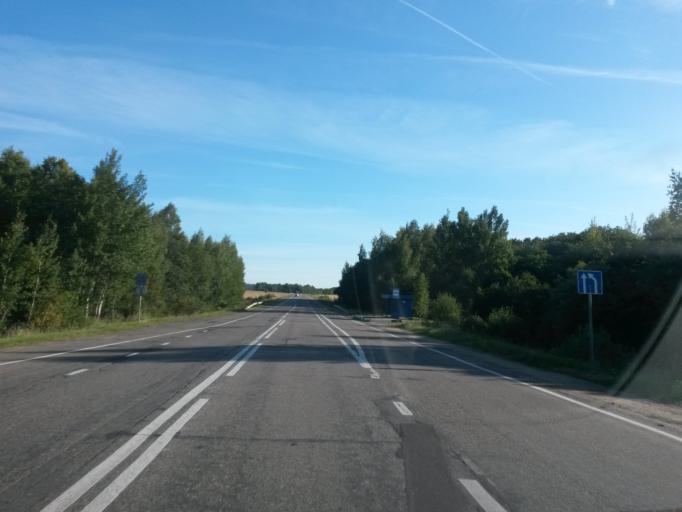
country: RU
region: Jaroslavl
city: Gavrilov-Yam
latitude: 57.4094
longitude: 39.9209
